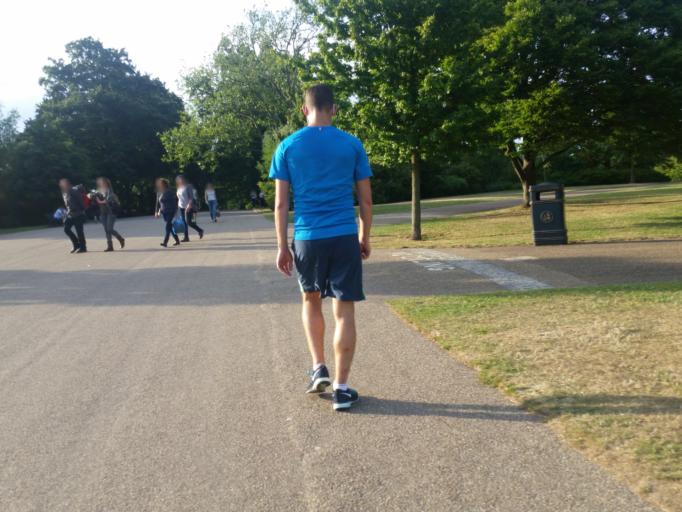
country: GB
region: England
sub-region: Greater London
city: Camden Town
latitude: 51.5329
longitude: -0.1505
